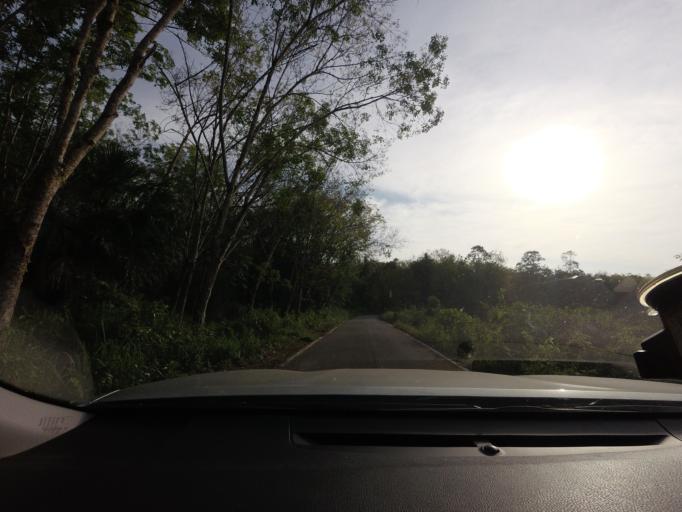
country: TH
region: Narathiwat
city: Ra-ngae
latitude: 6.3011
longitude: 101.7714
